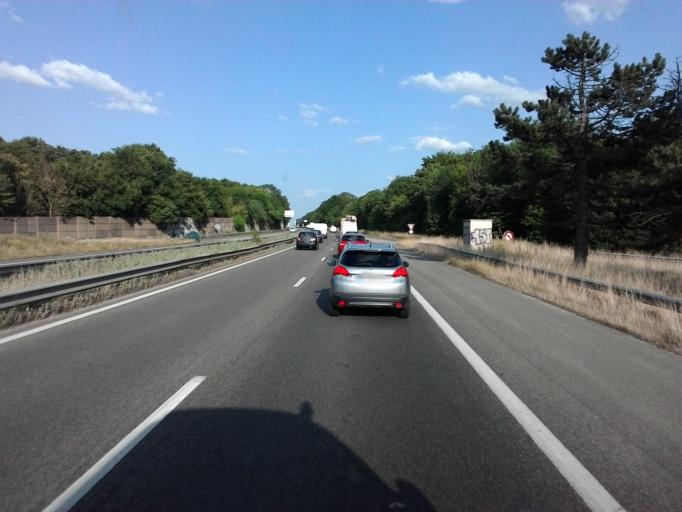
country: FR
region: Lorraine
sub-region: Departement de Meurthe-et-Moselle
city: Chavigny
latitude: 48.6460
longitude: 6.1417
